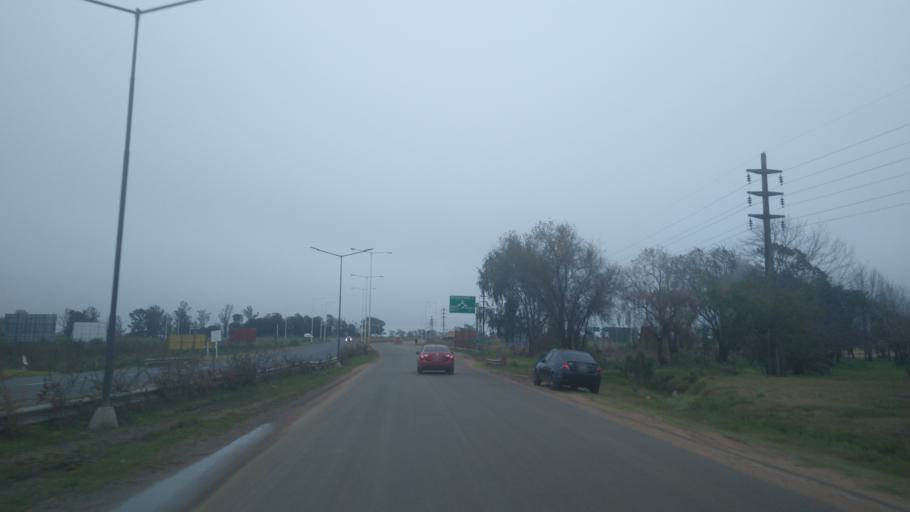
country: AR
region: Entre Rios
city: Chajari
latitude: -30.7616
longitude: -58.0168
